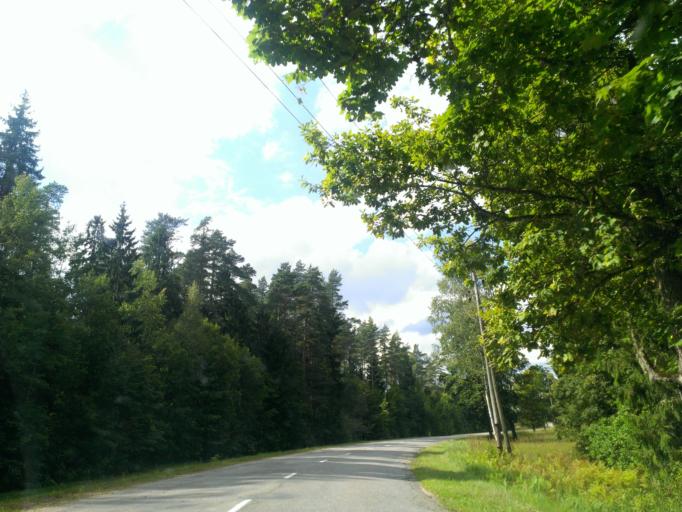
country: LV
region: Garkalne
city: Garkalne
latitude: 56.9663
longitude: 24.4901
